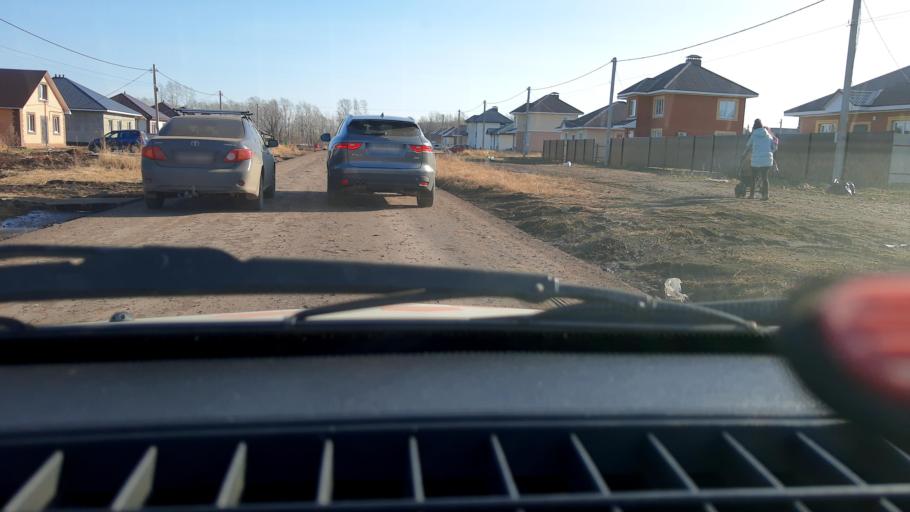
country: RU
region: Bashkortostan
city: Kabakovo
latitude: 54.6257
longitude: 56.1368
